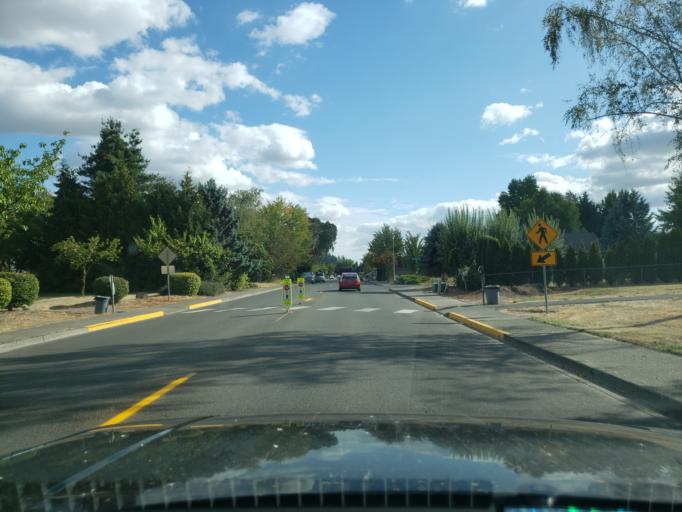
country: US
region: Oregon
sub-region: Yamhill County
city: McMinnville
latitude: 45.2049
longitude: -123.2197
